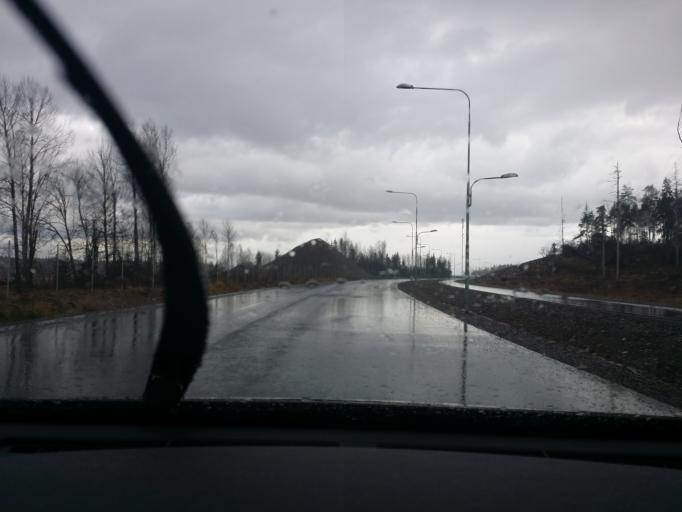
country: SE
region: Soedermanland
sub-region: Eskilstuna Kommun
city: Arla
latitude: 59.3545
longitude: 16.7018
